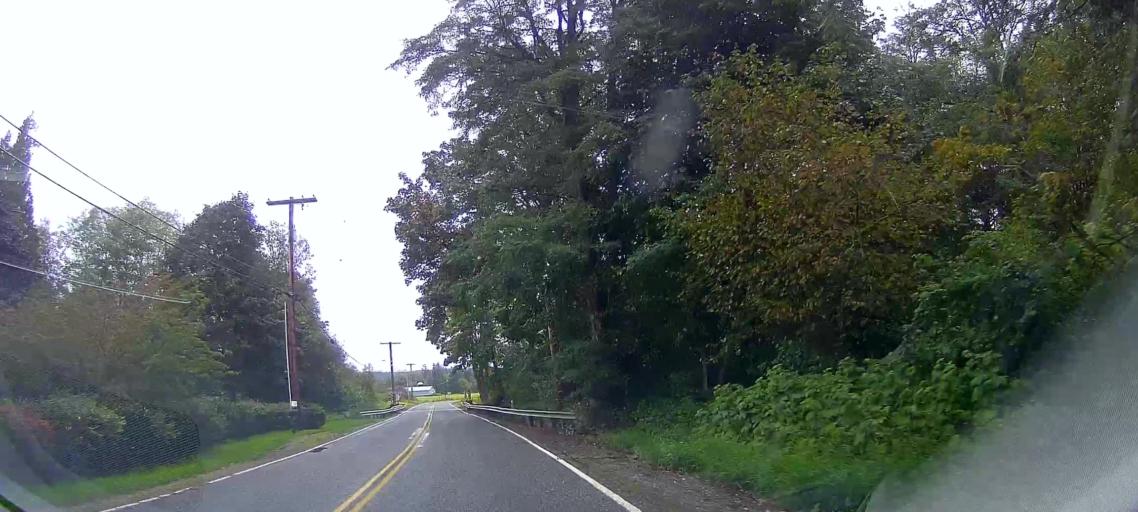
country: US
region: Washington
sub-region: Skagit County
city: Sedro-Woolley
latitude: 48.5275
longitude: -122.0248
